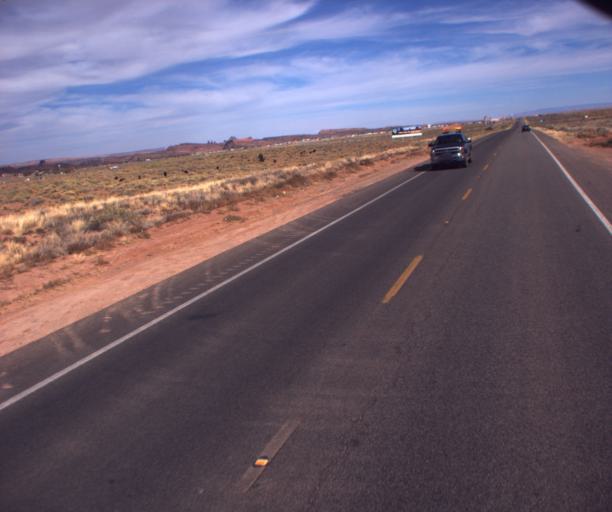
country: US
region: Arizona
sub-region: Navajo County
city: Kayenta
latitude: 36.7031
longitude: -110.2779
